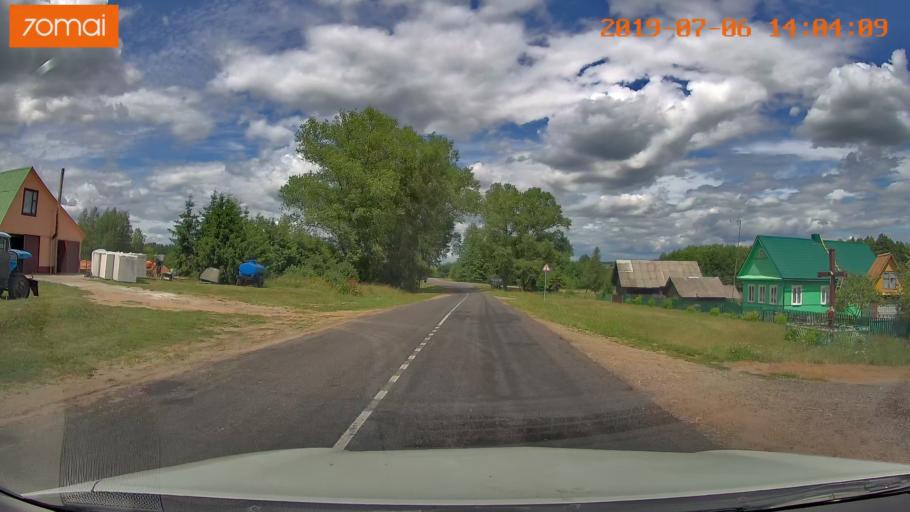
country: BY
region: Minsk
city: Ivyanyets
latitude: 53.8366
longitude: 26.8004
